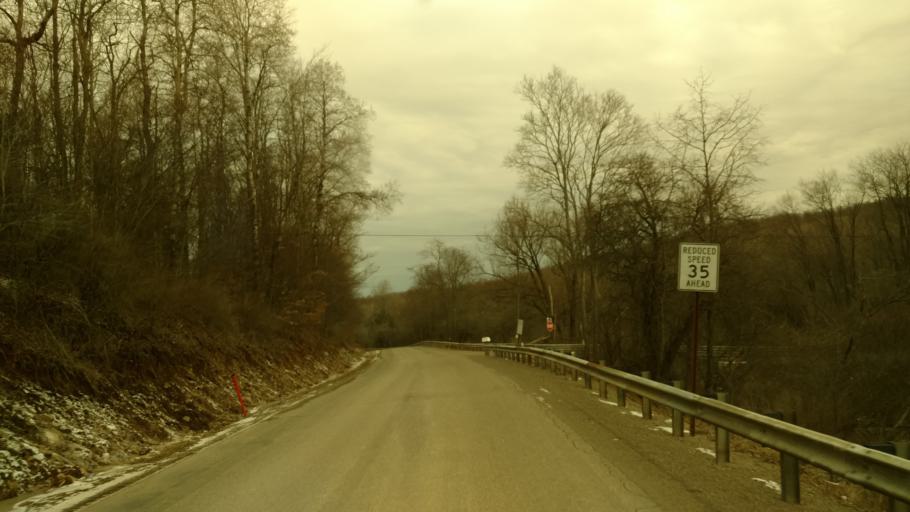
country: US
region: New York
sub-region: Allegany County
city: Andover
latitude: 41.9369
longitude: -77.8042
